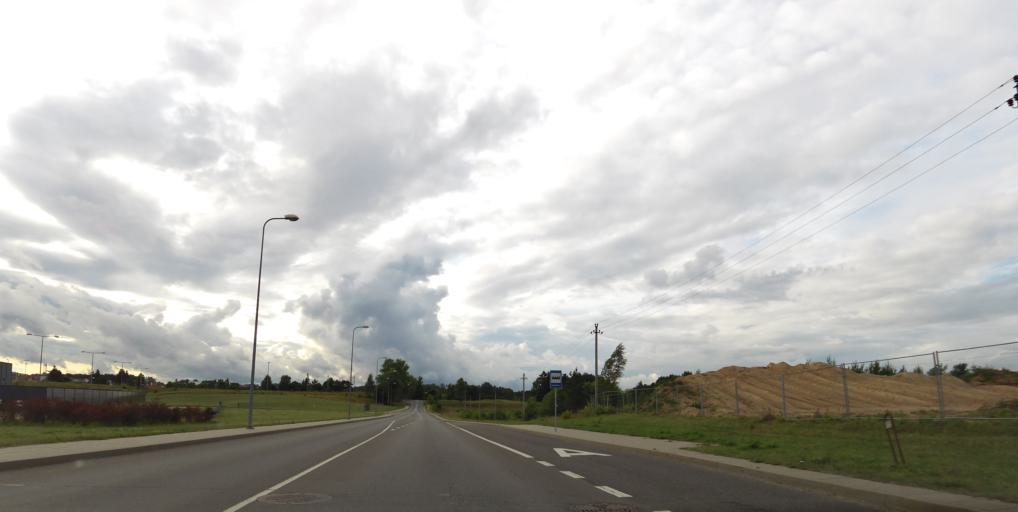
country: LT
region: Vilnius County
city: Justiniskes
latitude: 54.7085
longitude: 25.2032
